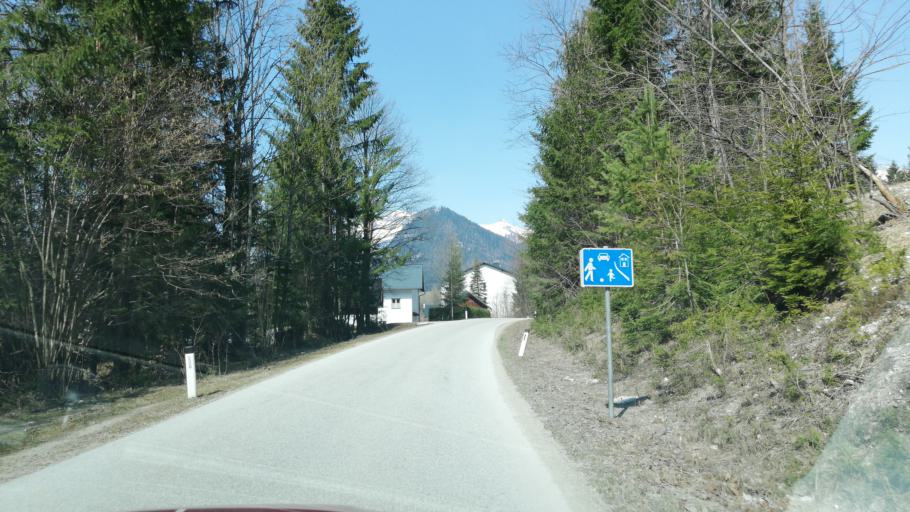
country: AT
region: Styria
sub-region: Politischer Bezirk Liezen
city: Bad Aussee
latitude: 47.5970
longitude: 13.7934
